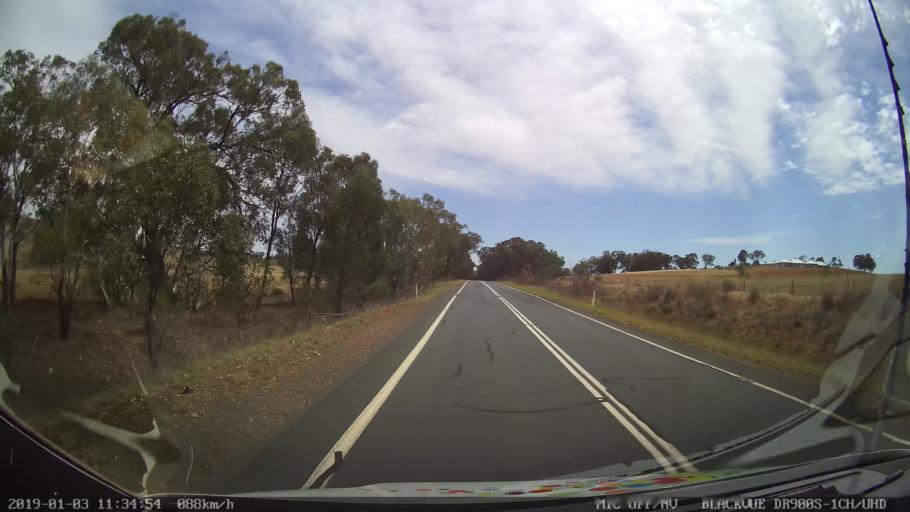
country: AU
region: New South Wales
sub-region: Weddin
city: Grenfell
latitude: -33.9294
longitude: 148.1603
